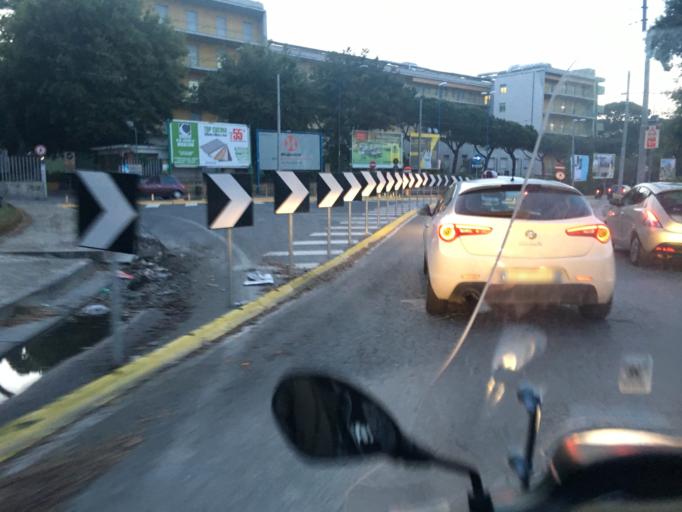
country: IT
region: Campania
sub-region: Provincia di Napoli
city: Napoli
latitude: 40.8660
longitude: 14.2272
